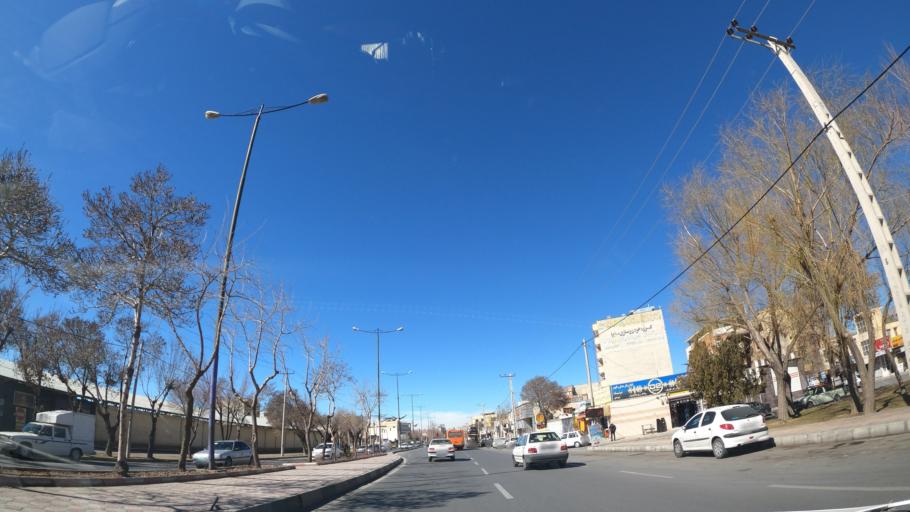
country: IR
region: Chahar Mahall va Bakhtiari
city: Shahrekord
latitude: 32.3141
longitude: 50.8752
